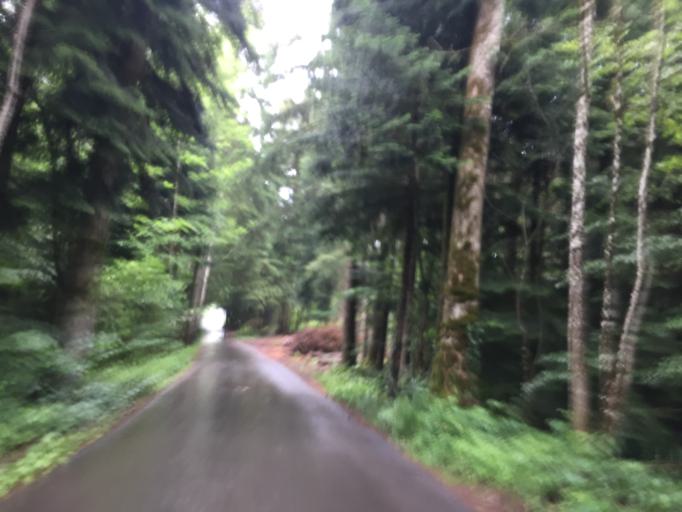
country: CH
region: Bern
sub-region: Bern-Mittelland District
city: Worb
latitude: 46.9104
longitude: 7.5925
